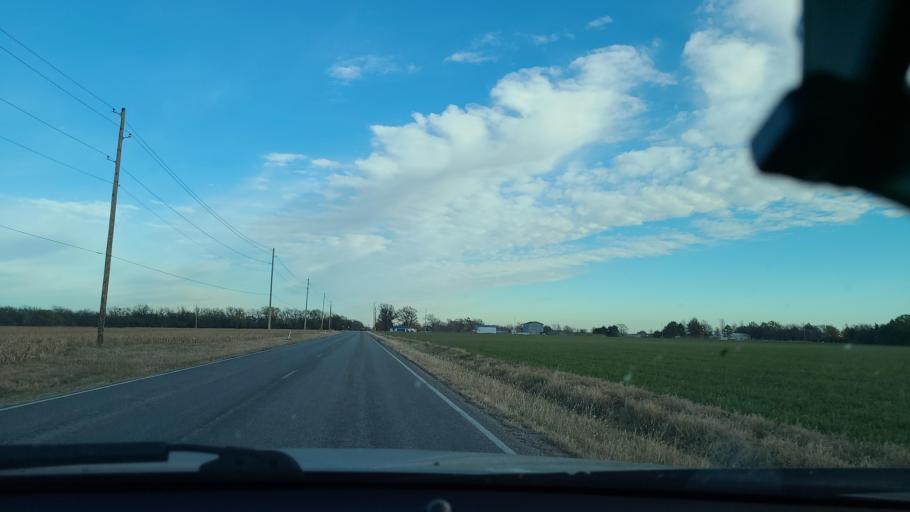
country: US
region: Kansas
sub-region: Sedgwick County
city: Goddard
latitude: 37.6498
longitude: -97.5391
